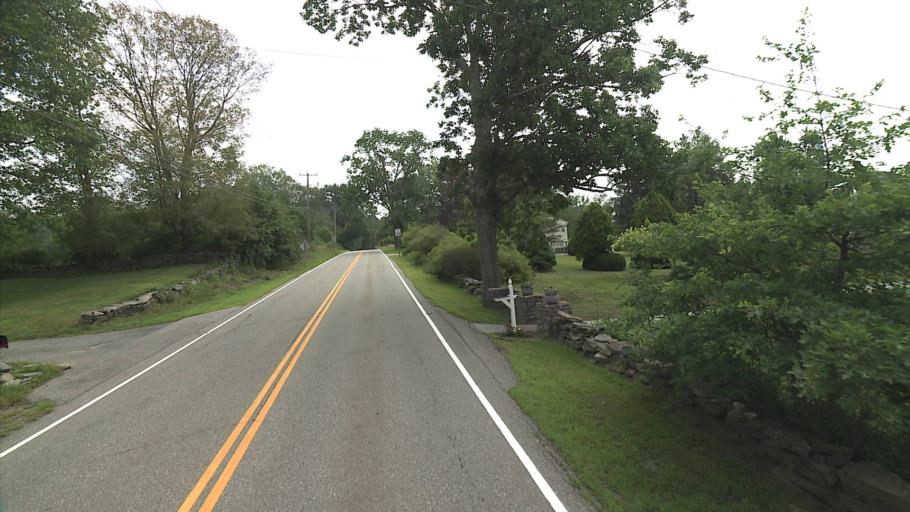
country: US
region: Connecticut
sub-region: Windham County
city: Wauregan
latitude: 41.7803
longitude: -71.9480
